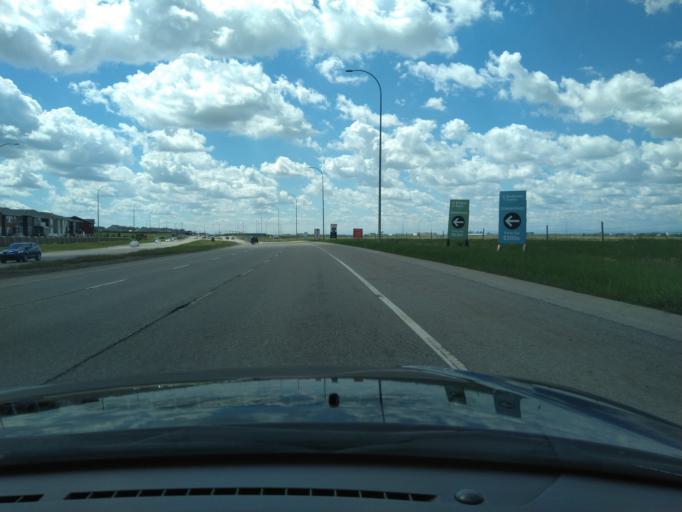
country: CA
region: Alberta
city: Airdrie
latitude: 51.1697
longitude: -113.9700
